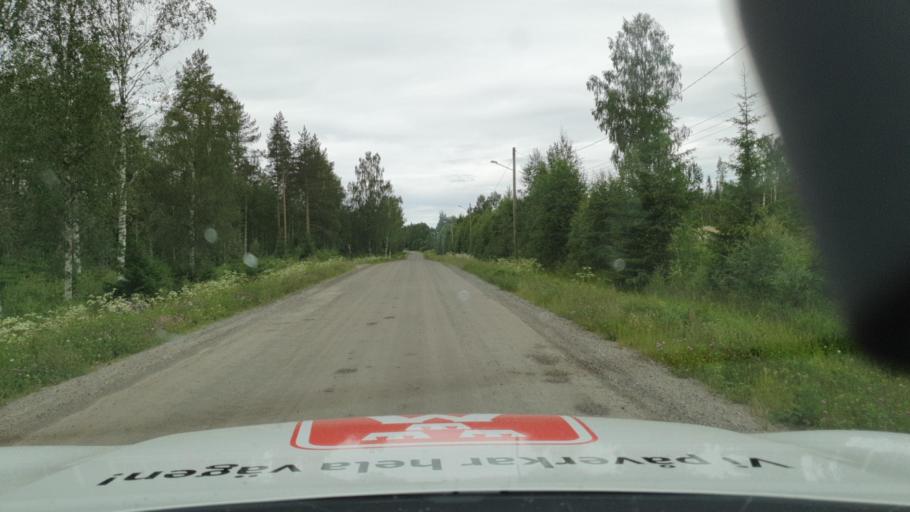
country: SE
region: Vaesterbotten
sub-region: Nordmalings Kommun
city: Nordmaling
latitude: 63.7765
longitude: 19.4001
